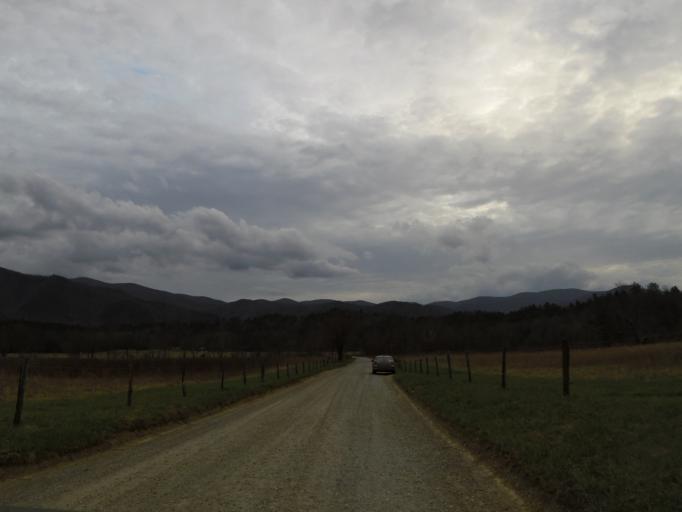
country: US
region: Tennessee
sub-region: Blount County
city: Wildwood
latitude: 35.5956
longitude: -83.8240
